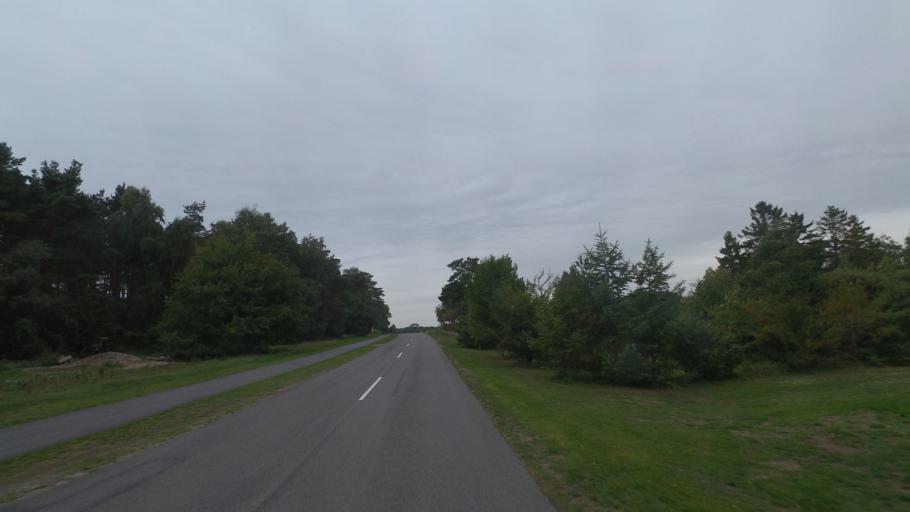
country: DK
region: Capital Region
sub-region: Bornholm Kommune
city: Akirkeby
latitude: 55.0027
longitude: 15.0213
